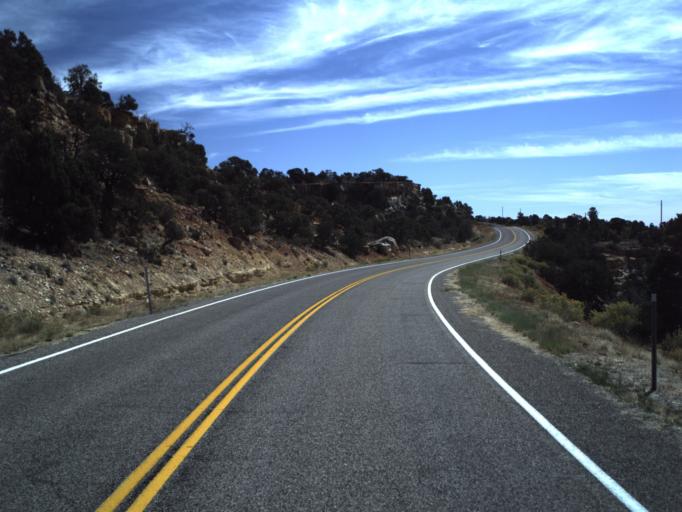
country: US
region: Utah
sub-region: Wayne County
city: Loa
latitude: 37.8918
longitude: -111.4521
